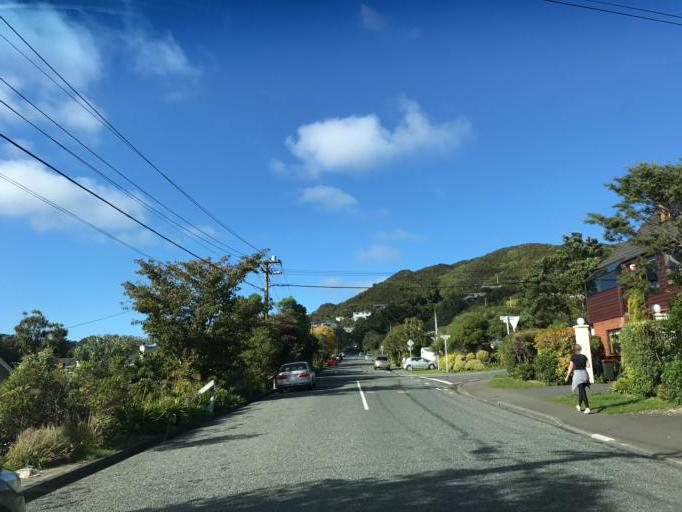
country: NZ
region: Wellington
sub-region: Wellington City
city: Kelburn
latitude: -41.2881
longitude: 174.7386
